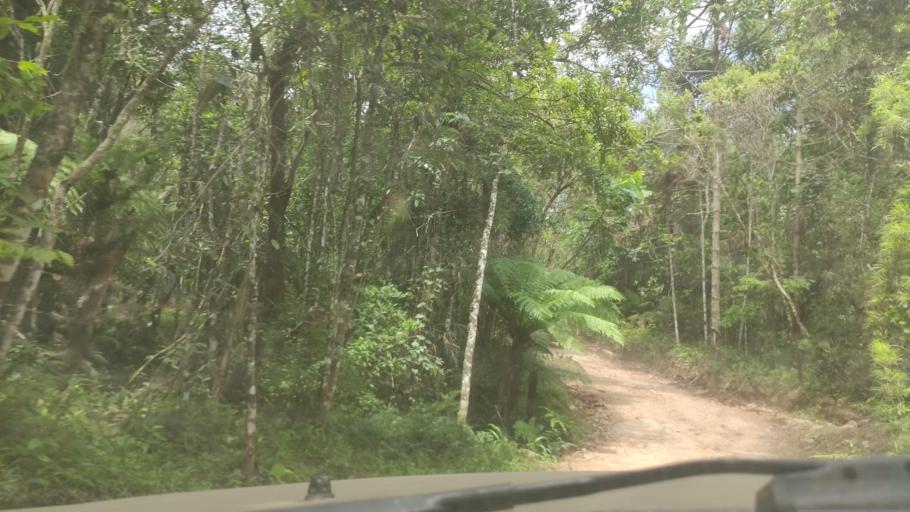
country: BR
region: Minas Gerais
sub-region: Cambui
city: Cambui
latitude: -22.6694
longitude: -45.9359
